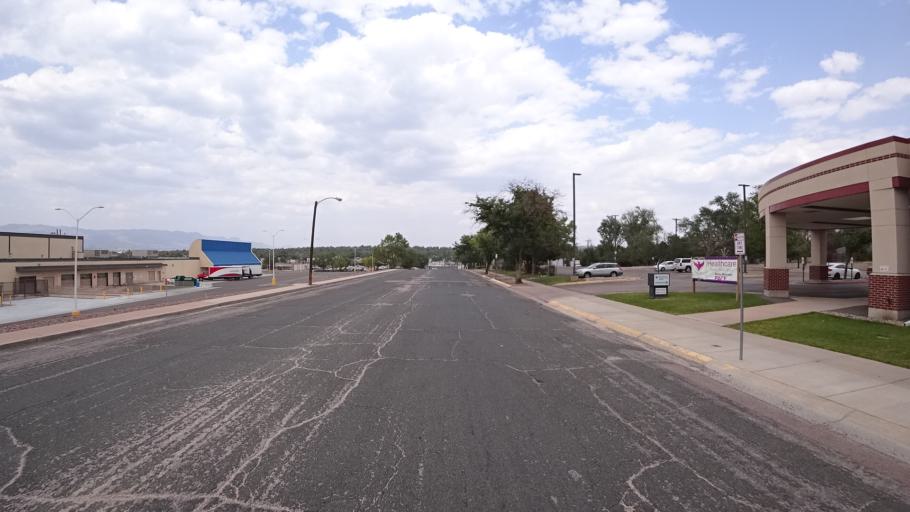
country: US
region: Colorado
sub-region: El Paso County
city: Colorado Springs
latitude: 38.8337
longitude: -104.7846
